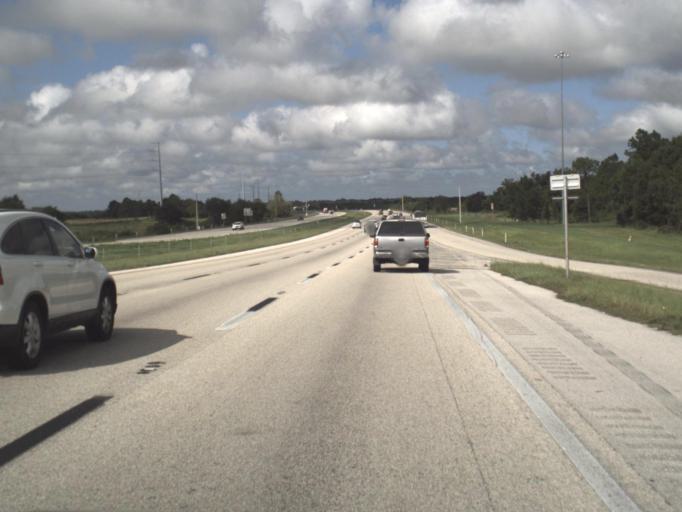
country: US
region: Florida
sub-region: Polk County
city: Gibsonia
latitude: 28.1398
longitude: -81.9006
